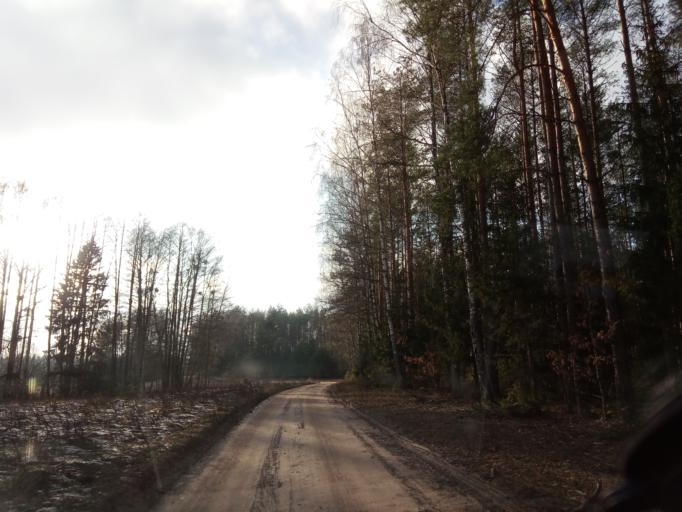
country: LT
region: Alytaus apskritis
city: Druskininkai
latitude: 53.9441
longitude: 24.2800
